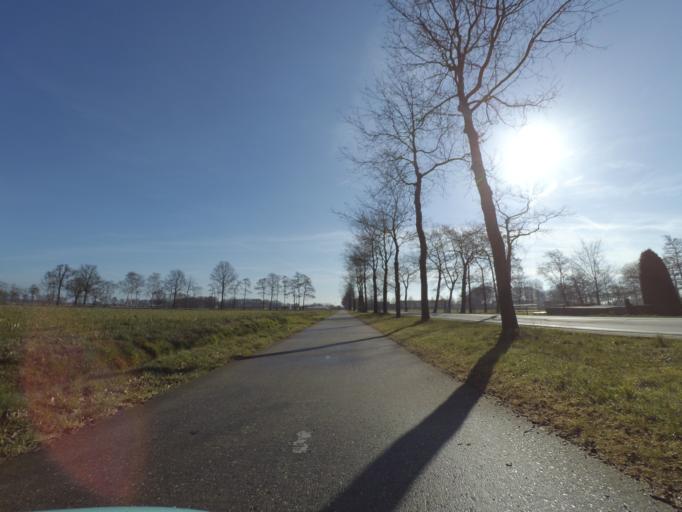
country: NL
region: Gelderland
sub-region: Gemeente Barneveld
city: Kootwijkerbroek
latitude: 52.1496
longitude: 5.6362
